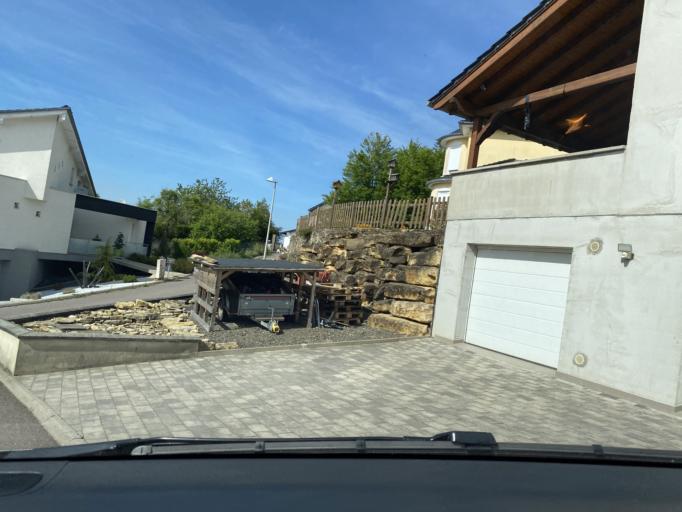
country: FR
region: Lorraine
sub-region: Departement de la Moselle
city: OEting
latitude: 49.1703
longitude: 6.9175
